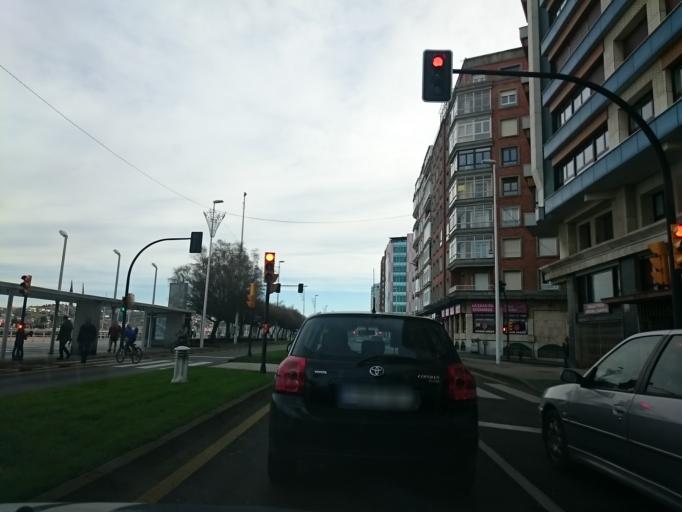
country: ES
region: Asturias
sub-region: Province of Asturias
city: Gijon
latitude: 43.5453
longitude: -5.6250
